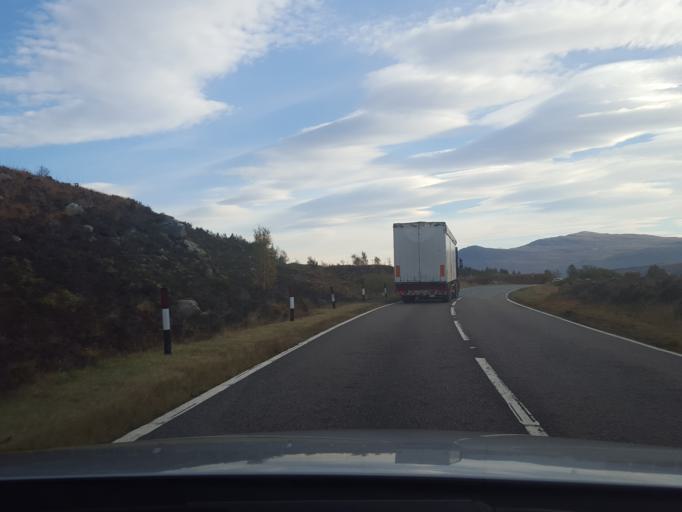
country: GB
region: Scotland
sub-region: Highland
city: Spean Bridge
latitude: 57.1482
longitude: -5.0116
